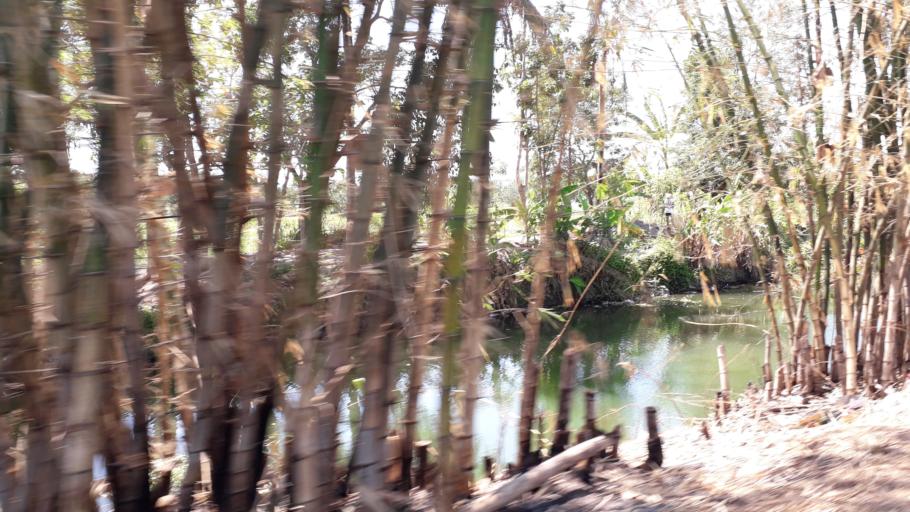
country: ID
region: Daerah Istimewa Yogyakarta
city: Pundong
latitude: -7.9498
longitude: 110.3277
